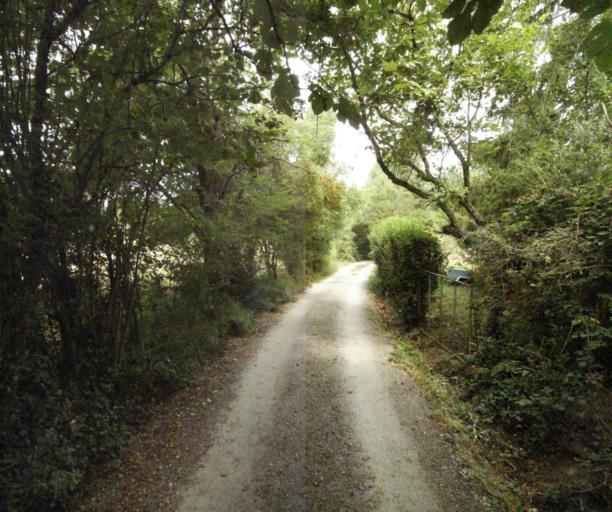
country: FR
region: Midi-Pyrenees
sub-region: Departement du Tarn
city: Soreze
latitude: 43.4486
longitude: 2.0666
